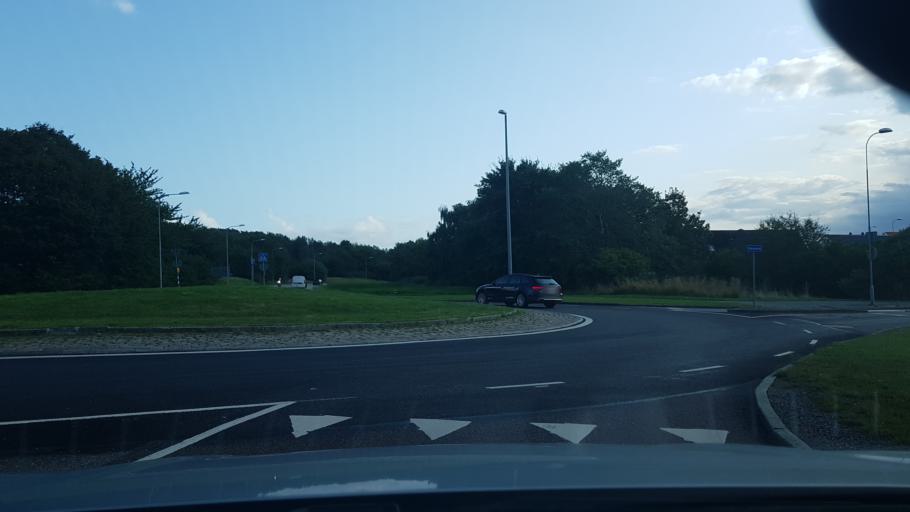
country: SE
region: Vaestra Goetaland
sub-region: Goteborg
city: Majorna
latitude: 57.6482
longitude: 11.8678
